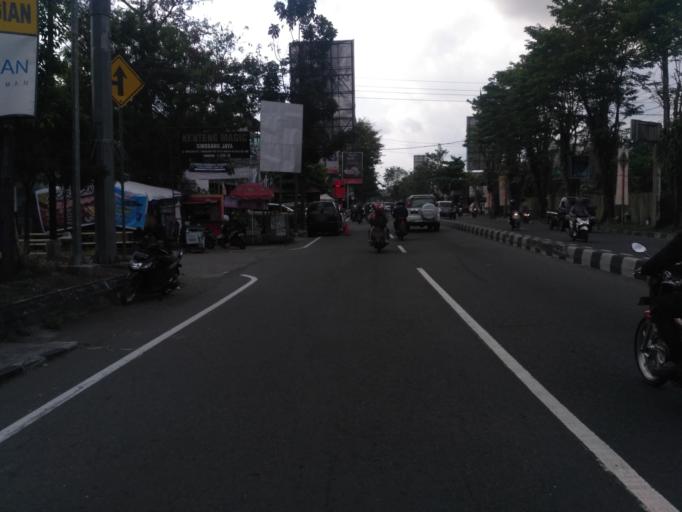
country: ID
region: Daerah Istimewa Yogyakarta
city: Melati
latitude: -7.7446
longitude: 110.3625
